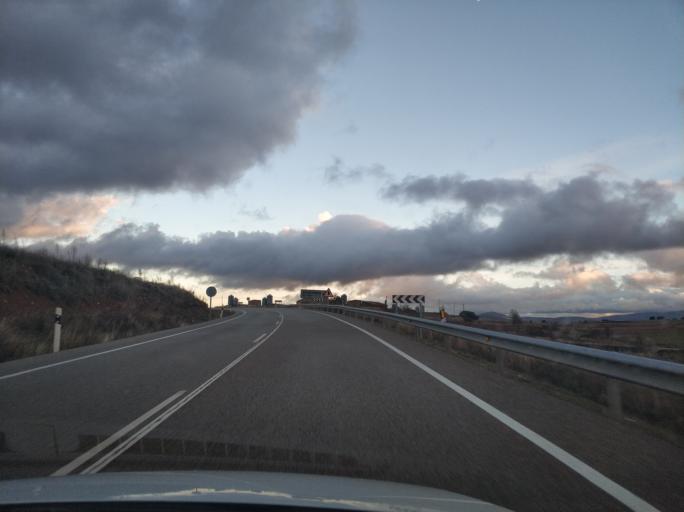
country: ES
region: Castille and Leon
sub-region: Provincia de Segovia
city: Ayllon
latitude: 41.4146
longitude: -3.4003
